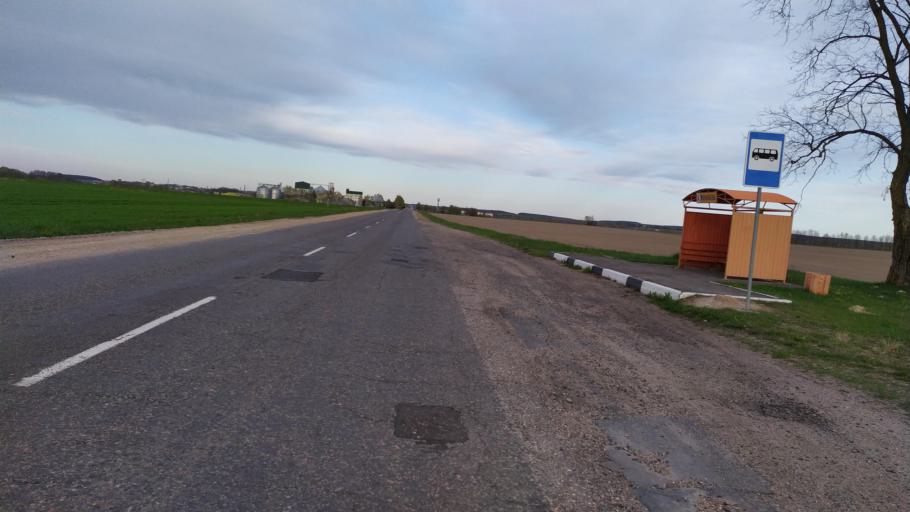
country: BY
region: Brest
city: Kamyanyets
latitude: 52.4034
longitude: 23.7679
